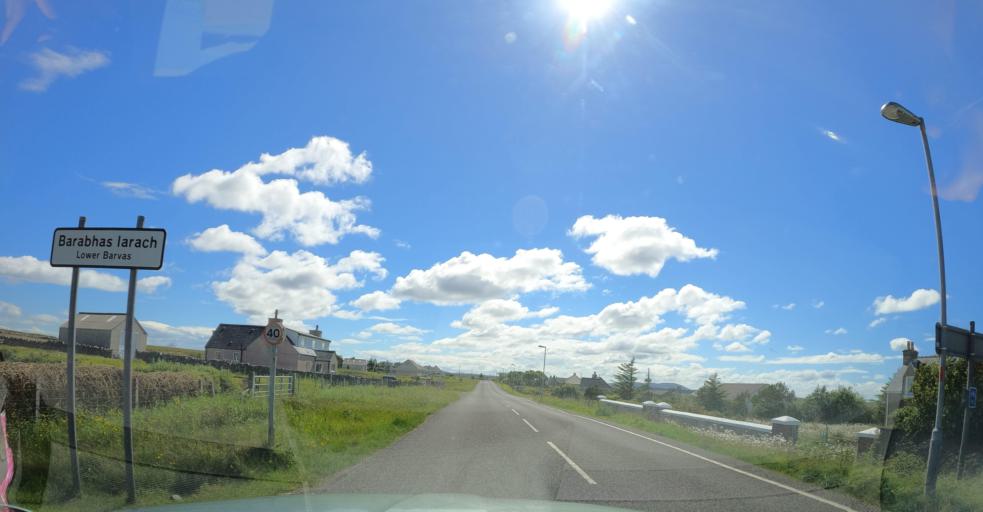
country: GB
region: Scotland
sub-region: Eilean Siar
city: Isle of Lewis
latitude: 58.3617
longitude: -6.5102
